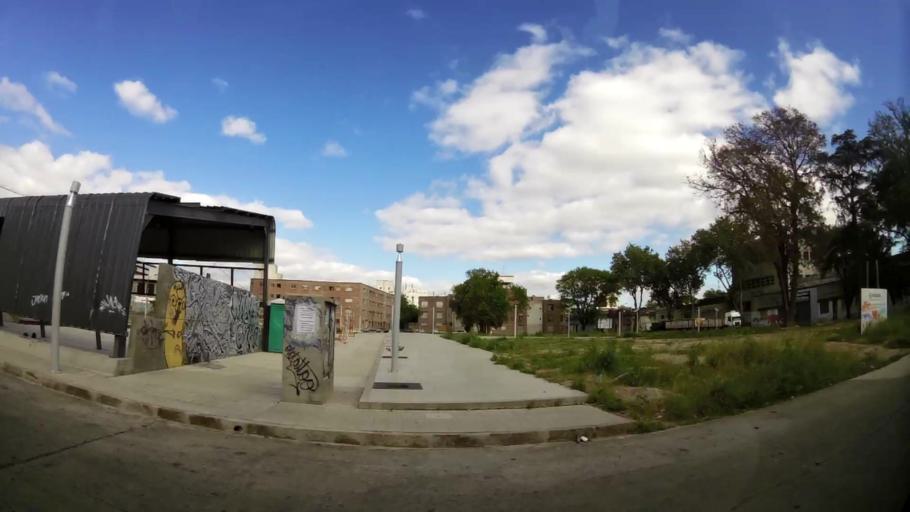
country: UY
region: Montevideo
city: Montevideo
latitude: -34.8866
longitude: -56.1814
